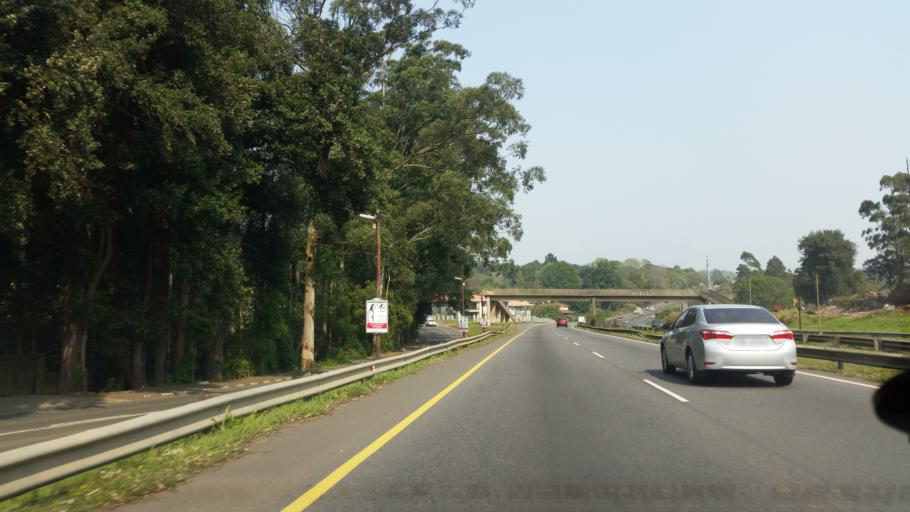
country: ZA
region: KwaZulu-Natal
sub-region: eThekwini Metropolitan Municipality
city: Mpumalanga
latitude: -29.7938
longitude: 30.8000
